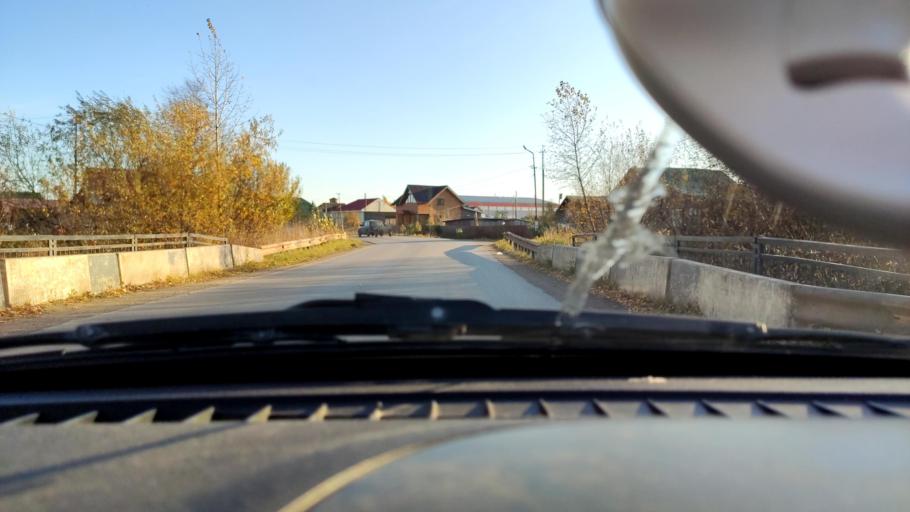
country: RU
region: Perm
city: Froly
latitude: 57.8855
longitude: 56.2575
